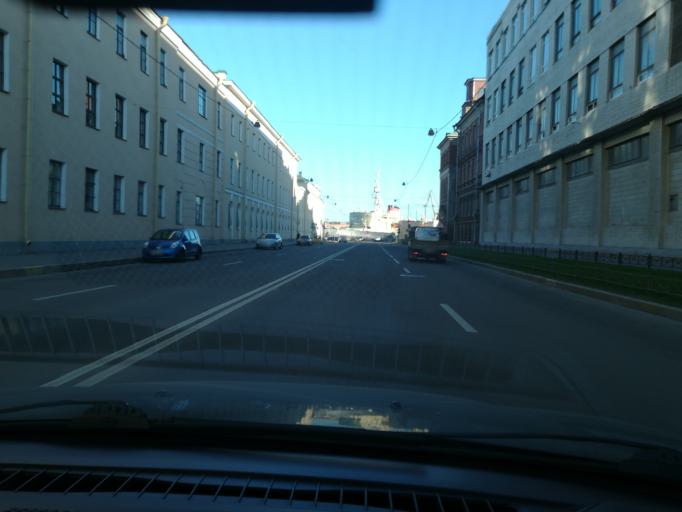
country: RU
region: St.-Petersburg
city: Vasyl'evsky Ostrov
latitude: 59.9298
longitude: 30.2665
